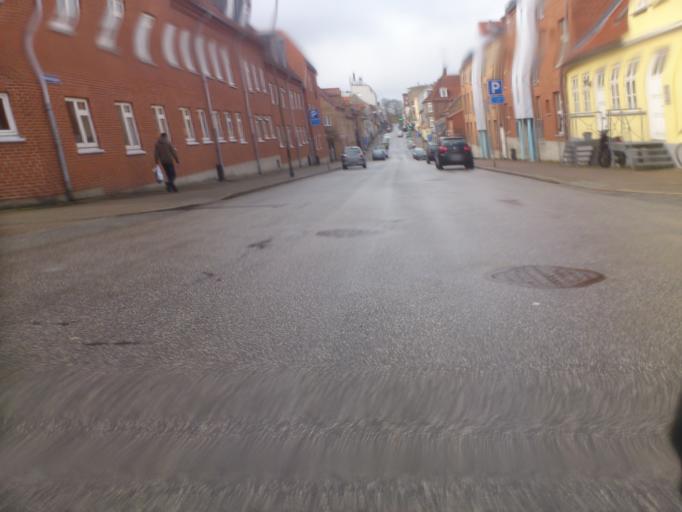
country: DK
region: South Denmark
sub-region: Fredericia Kommune
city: Fredericia
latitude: 55.5671
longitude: 9.7627
